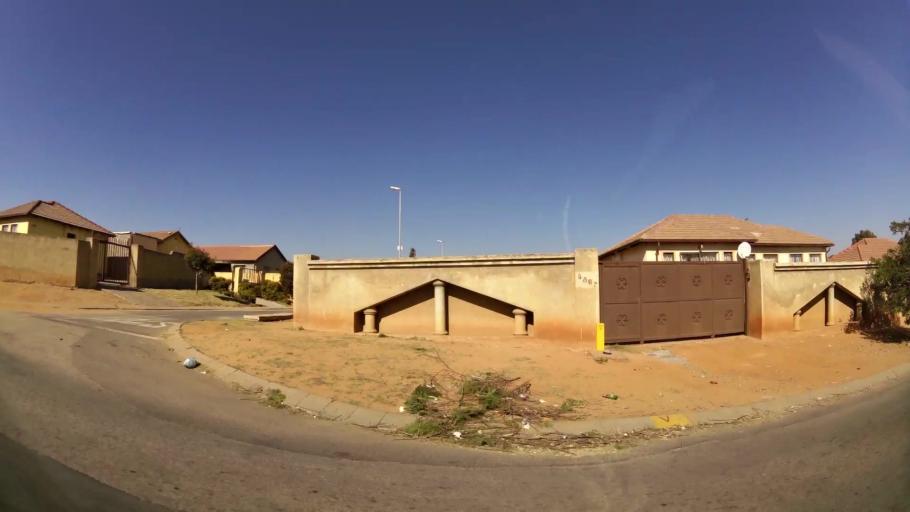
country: ZA
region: Gauteng
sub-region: Ekurhuleni Metropolitan Municipality
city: Tembisa
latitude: -26.0437
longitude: 28.1997
